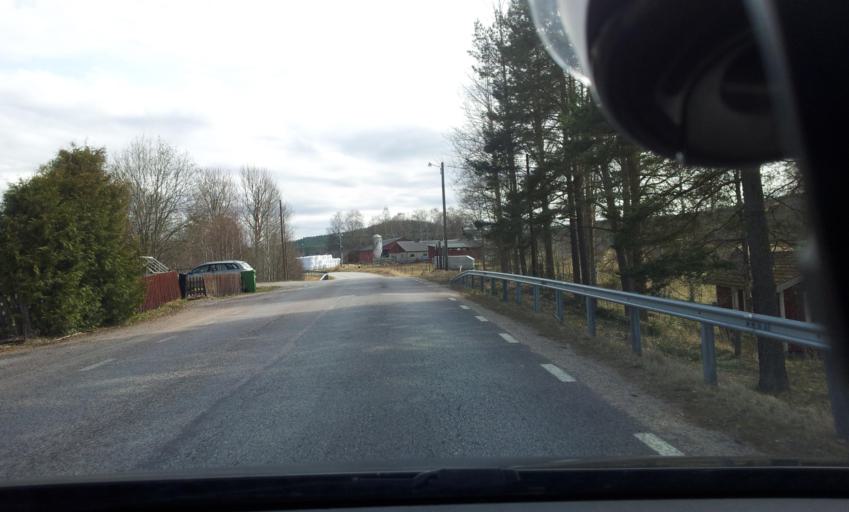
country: SE
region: Gaevleborg
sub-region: Ljusdals Kommun
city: Farila
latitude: 61.7770
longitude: 15.9491
